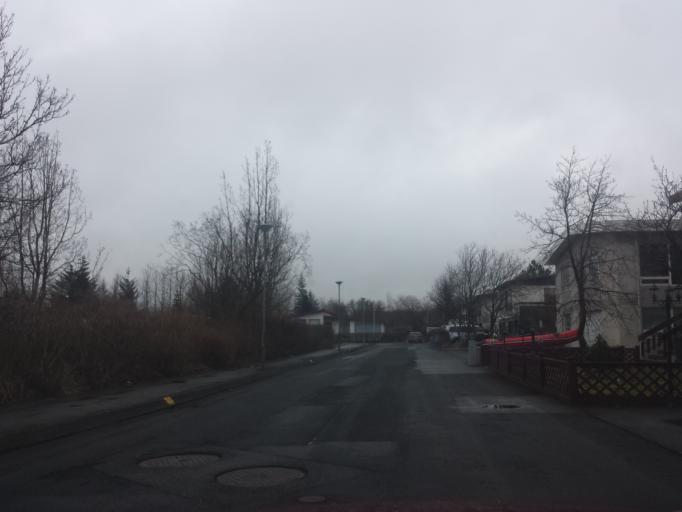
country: IS
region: Capital Region
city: Reykjavik
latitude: 64.1124
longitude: -21.8570
